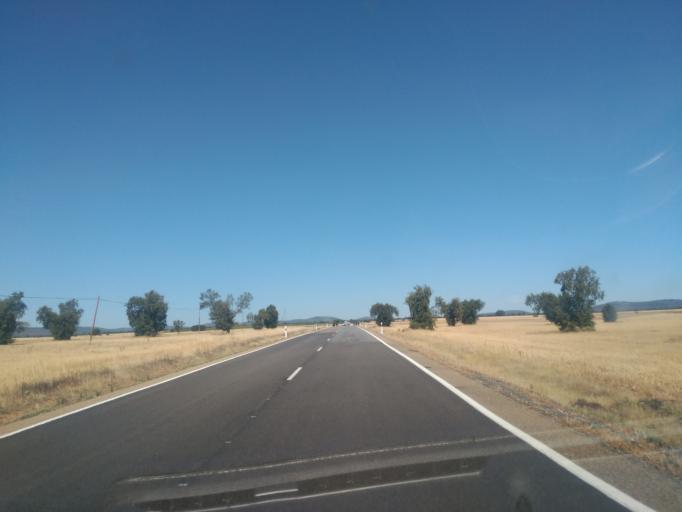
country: ES
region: Castille and Leon
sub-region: Provincia de Zamora
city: Pozuelo de Tabara
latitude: 41.7937
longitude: -5.9081
